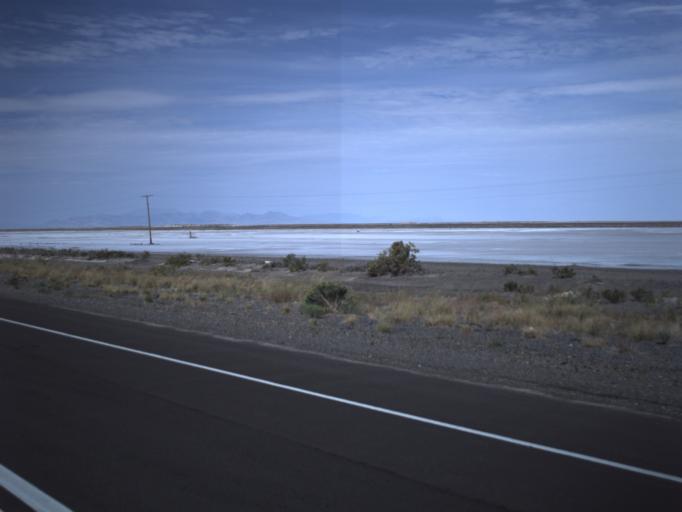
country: US
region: Utah
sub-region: Tooele County
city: Wendover
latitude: 40.7274
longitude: -113.2658
